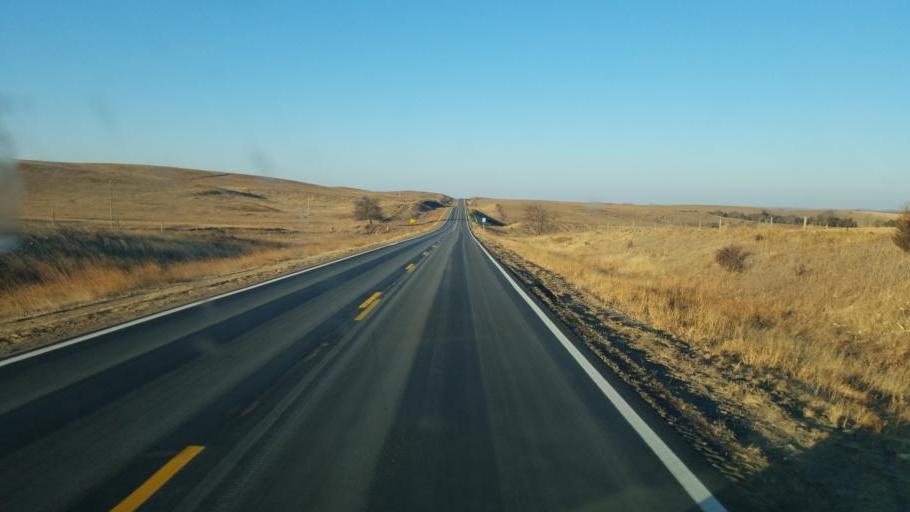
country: US
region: Nebraska
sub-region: Knox County
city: Center
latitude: 42.5970
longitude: -97.8192
